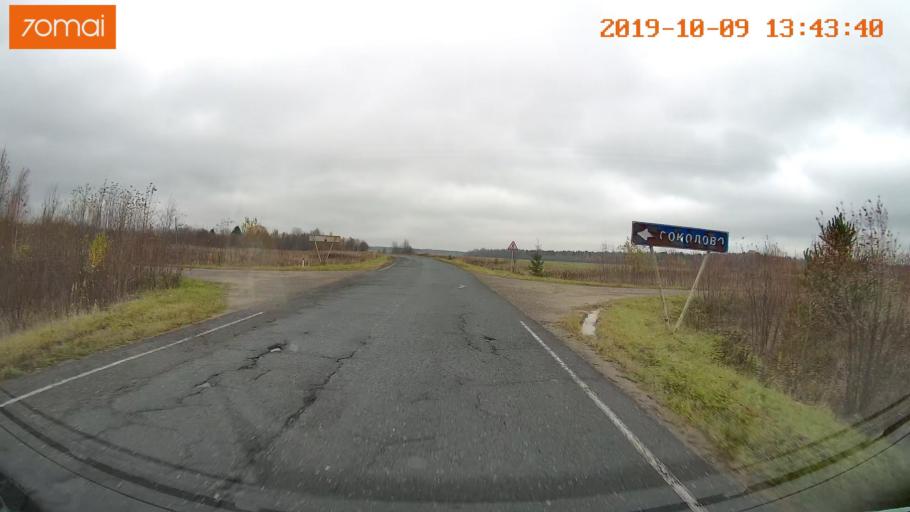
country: RU
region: Kostroma
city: Buy
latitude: 58.3589
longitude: 41.2029
